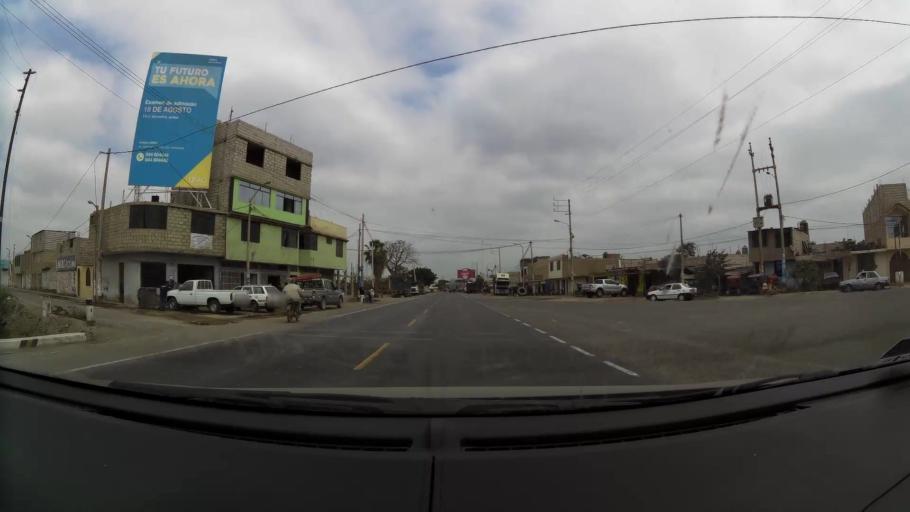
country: PE
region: La Libertad
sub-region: Ascope
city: Chocope
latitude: -7.7931
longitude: -79.2186
